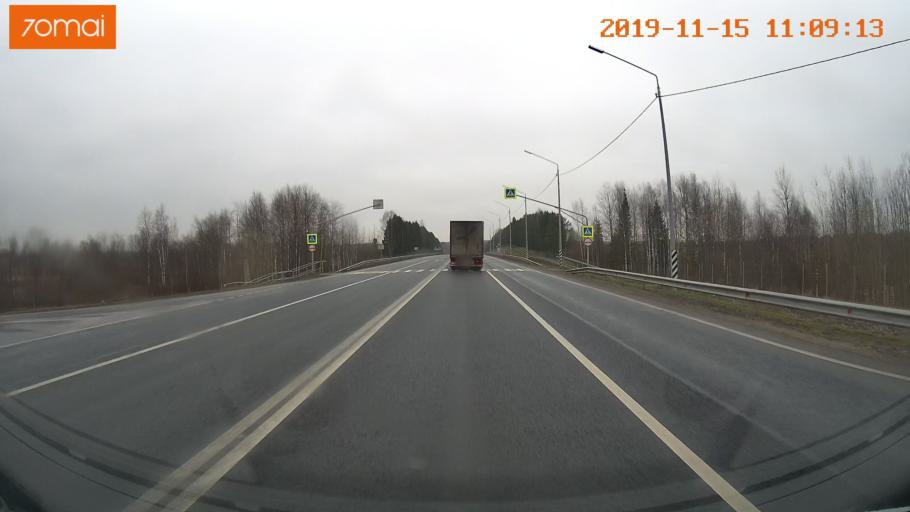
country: RU
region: Vologda
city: Chebsara
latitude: 59.1204
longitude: 39.0928
